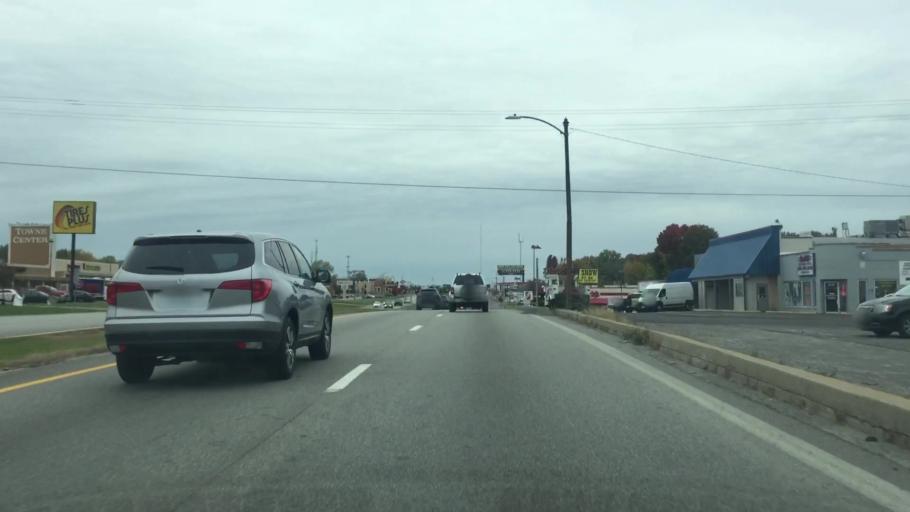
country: US
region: Missouri
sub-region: Jackson County
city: Raytown
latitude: 38.9952
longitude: -94.4743
